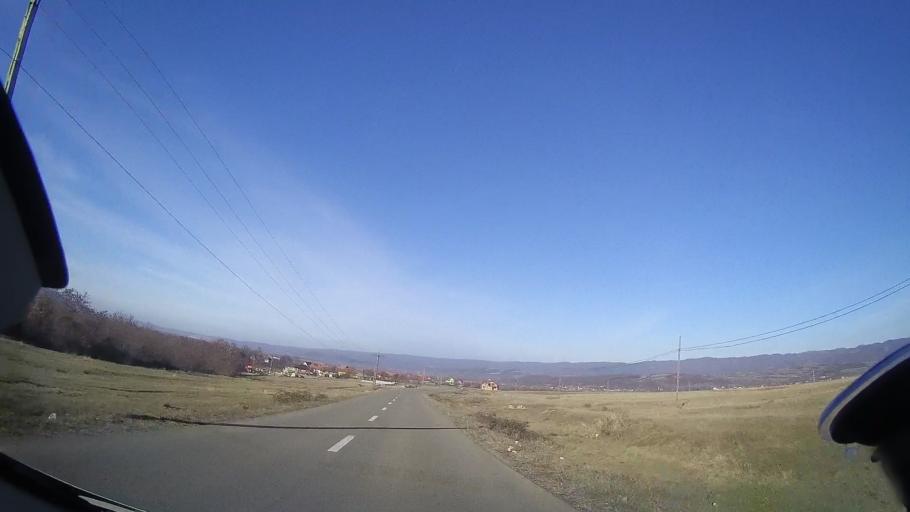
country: RO
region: Bihor
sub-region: Comuna Vadu Crisului
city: Vadu Crisului
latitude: 46.9810
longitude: 22.5316
